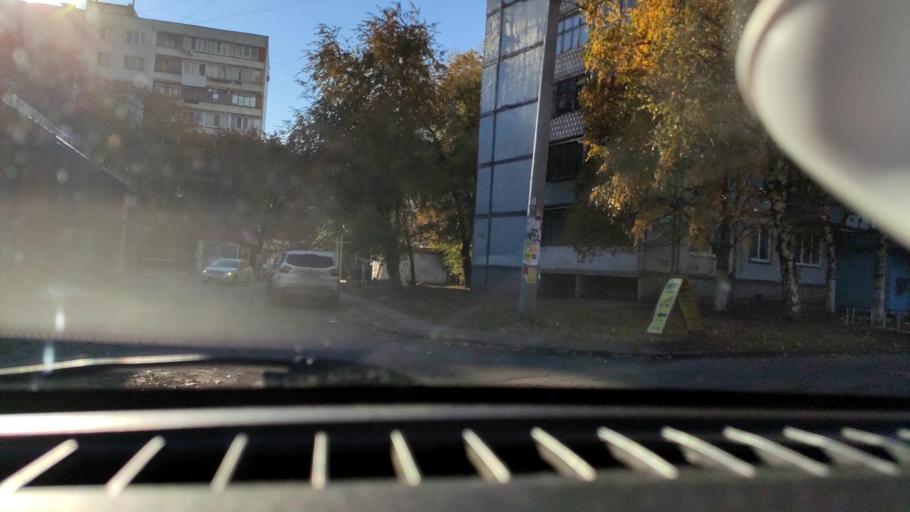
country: RU
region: Samara
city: Samara
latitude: 53.2397
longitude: 50.2082
